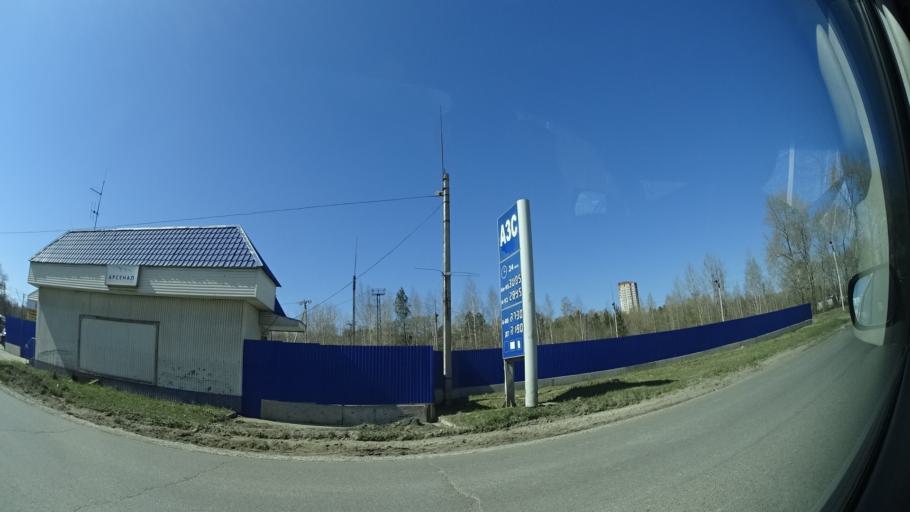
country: RU
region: Perm
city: Perm
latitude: 58.1090
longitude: 56.3219
